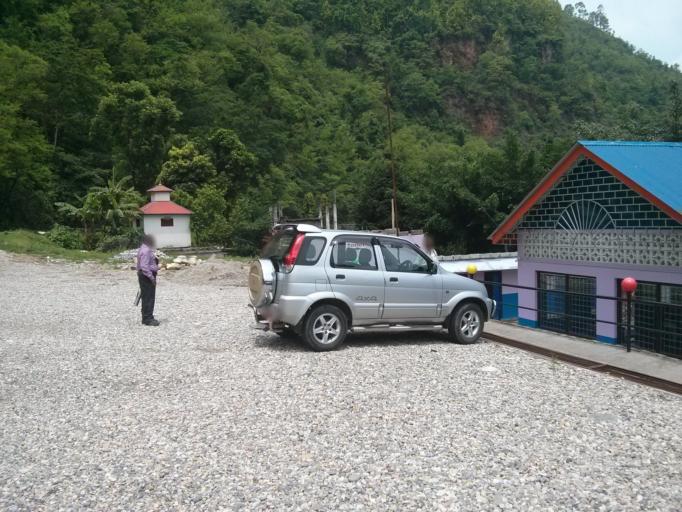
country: NP
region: Central Region
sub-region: Narayani Zone
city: Bharatpur
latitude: 27.8069
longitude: 84.8193
